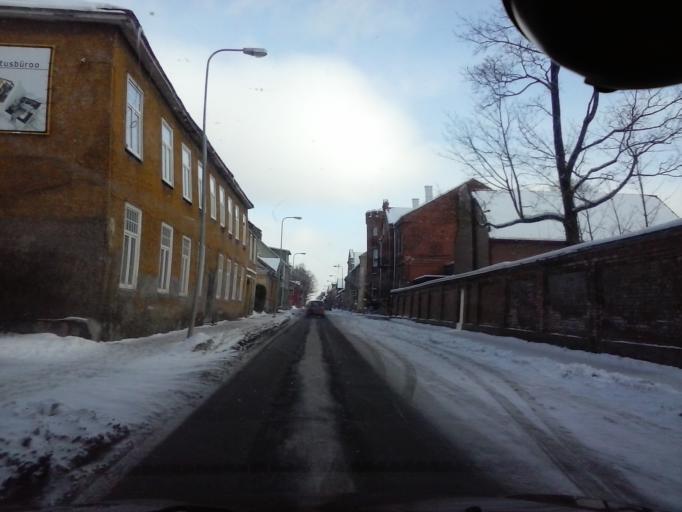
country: EE
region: Viljandimaa
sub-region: Viljandi linn
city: Viljandi
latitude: 58.3667
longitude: 25.6021
